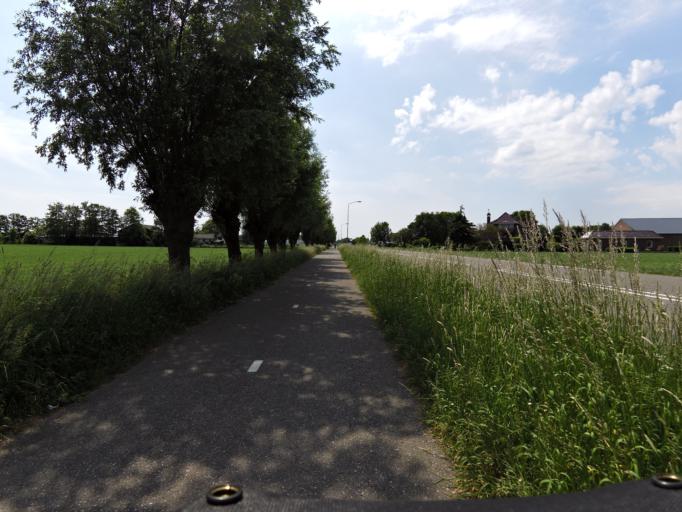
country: NL
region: North Brabant
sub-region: Gemeente Aalburg
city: Aalburg
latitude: 51.8089
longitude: 5.0879
